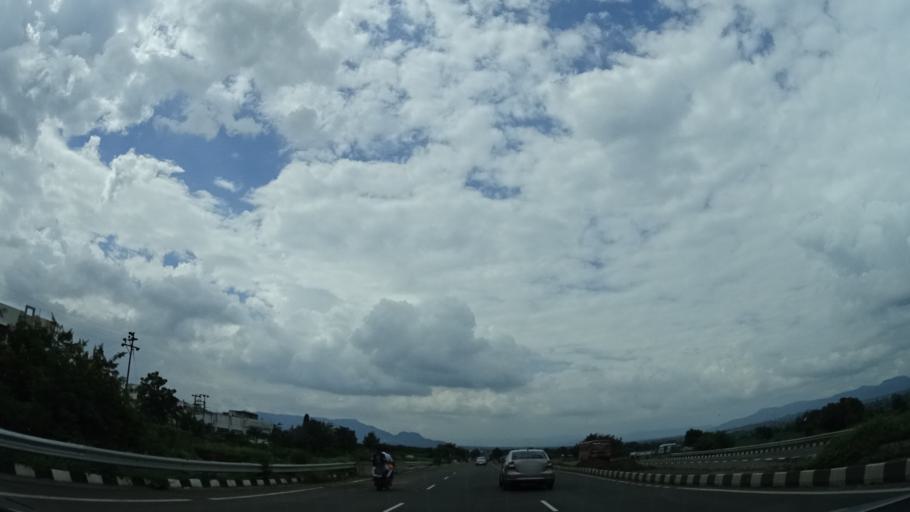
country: IN
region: Maharashtra
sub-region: Satara Division
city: Satara
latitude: 17.7959
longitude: 73.9778
